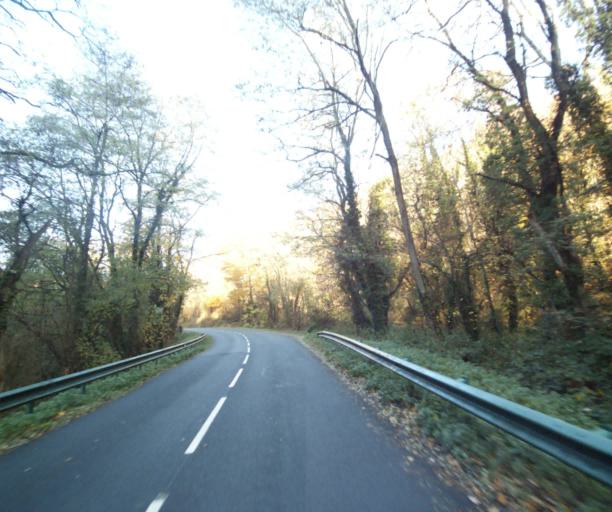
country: FR
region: Auvergne
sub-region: Departement du Puy-de-Dome
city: Nohanent
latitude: 45.8065
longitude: 3.0454
